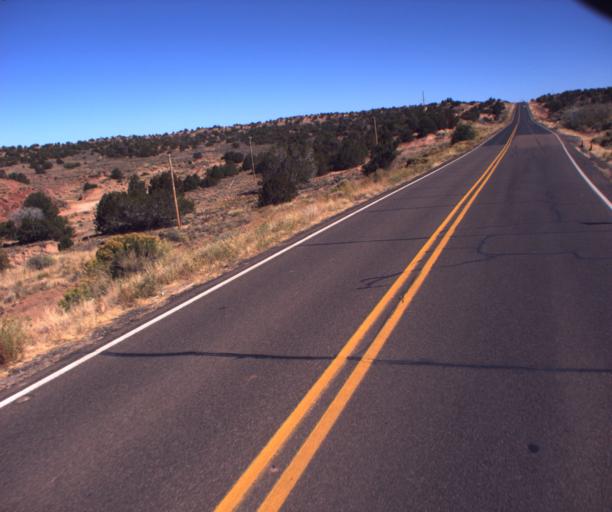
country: US
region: Arizona
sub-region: Apache County
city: Ganado
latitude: 35.7097
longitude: -109.5300
